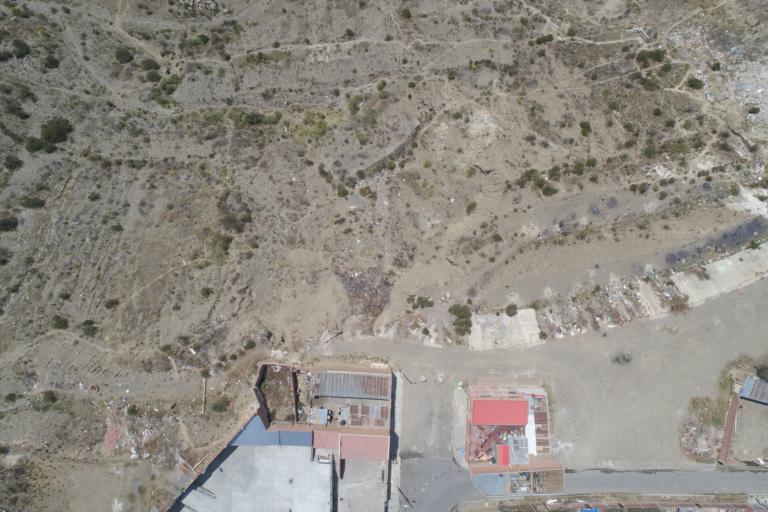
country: BO
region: La Paz
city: La Paz
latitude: -16.5039
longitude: -68.1006
